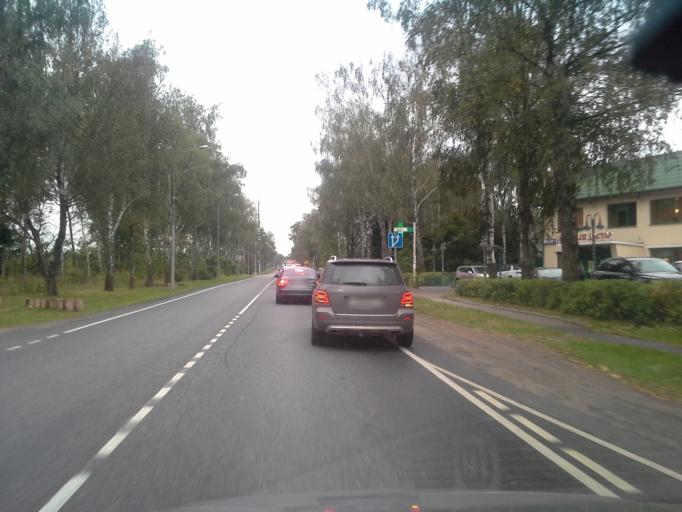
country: RU
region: Moskovskaya
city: Nikolina Gora
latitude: 55.7198
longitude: 37.0724
